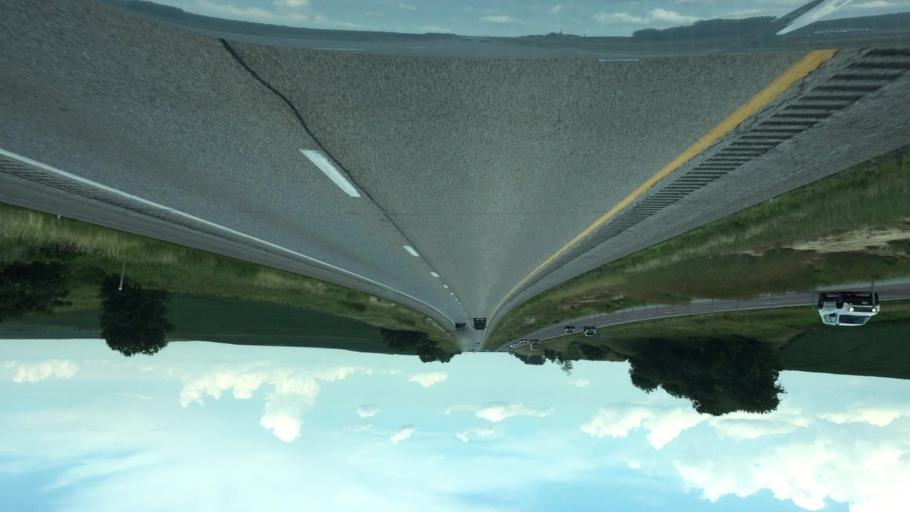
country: US
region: Iowa
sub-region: Iowa County
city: Marengo
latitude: 41.6951
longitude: -92.1384
